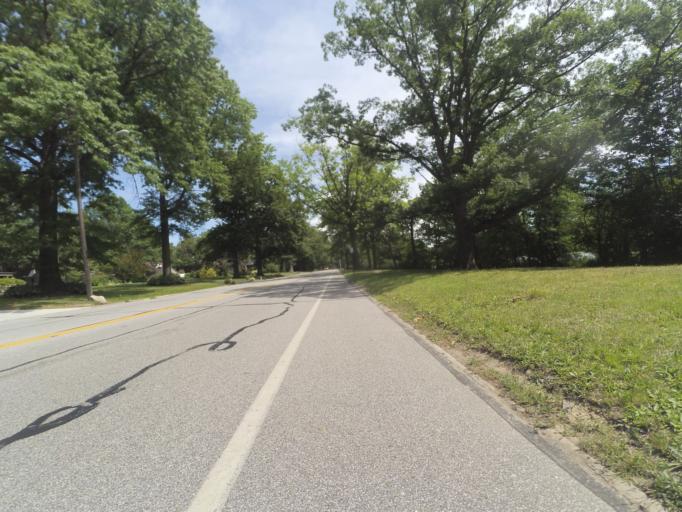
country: US
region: Ohio
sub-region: Cuyahoga County
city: Cleveland Heights
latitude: 41.4904
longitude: -81.5812
